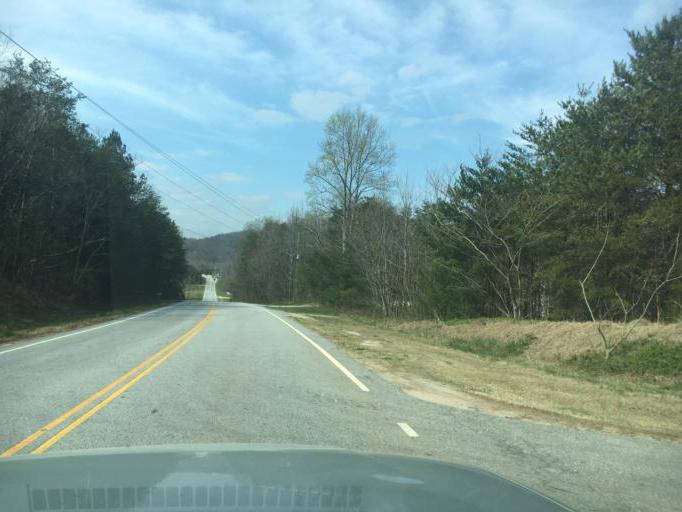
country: US
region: South Carolina
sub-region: Greenville County
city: Tigerville
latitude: 35.1198
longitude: -82.3417
